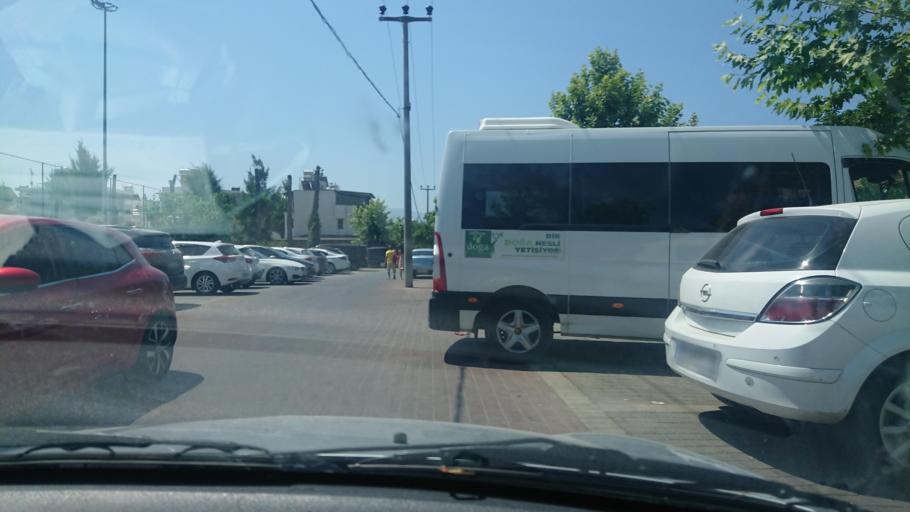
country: TR
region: Aydin
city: Kusadasi
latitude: 37.8005
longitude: 27.2728
